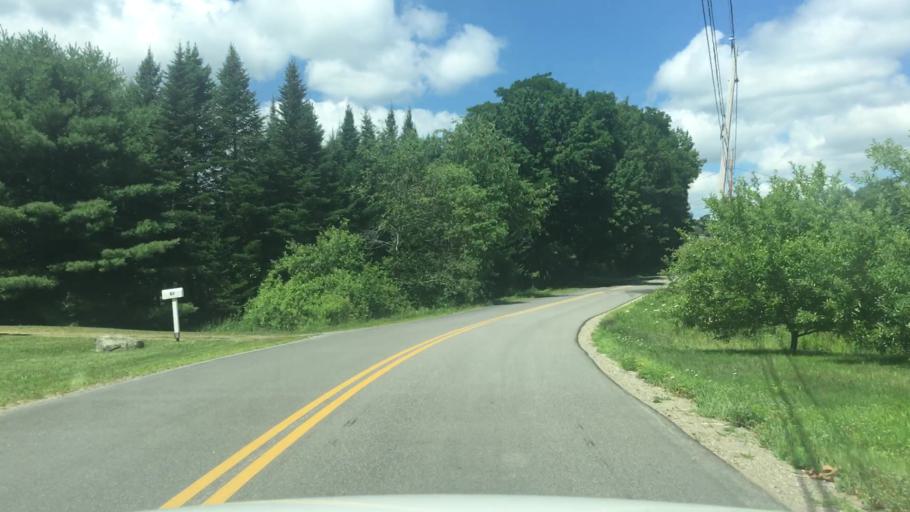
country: US
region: Maine
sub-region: Waldo County
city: Belfast
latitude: 44.4079
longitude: -69.0342
